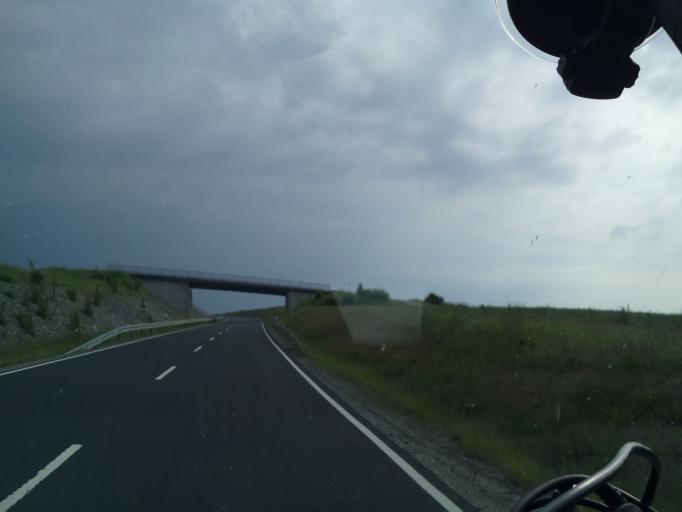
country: DE
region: Bavaria
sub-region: Regierungsbezirk Unterfranken
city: Hendungen
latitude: 50.4195
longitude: 10.3342
